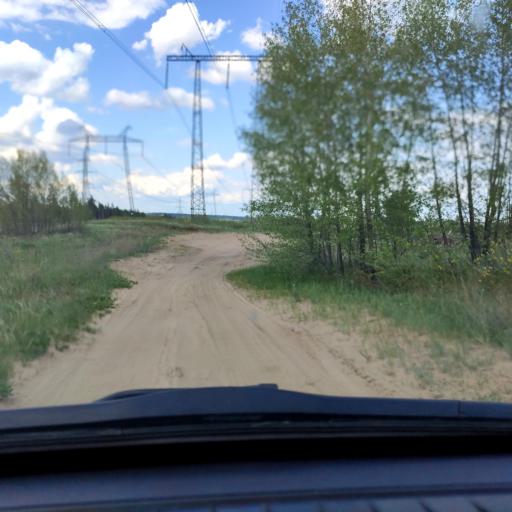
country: RU
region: Samara
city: Zhigulevsk
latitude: 53.5370
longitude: 49.5481
